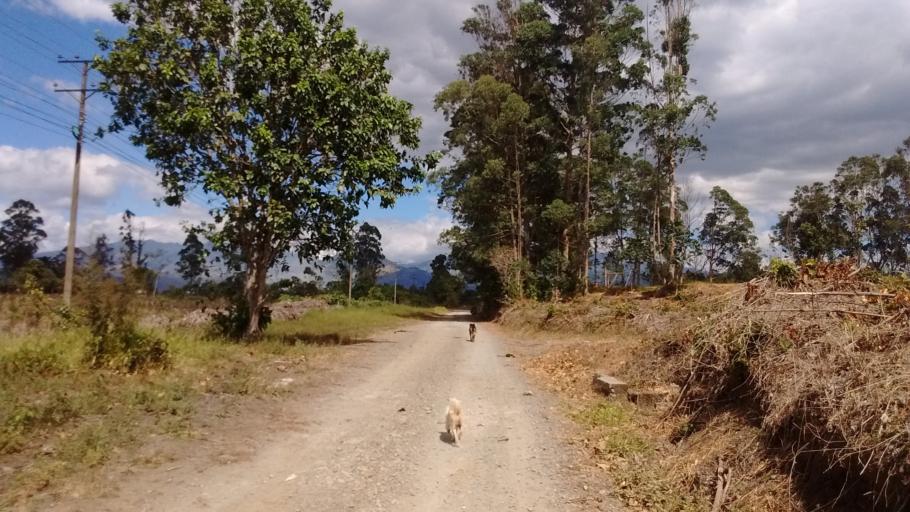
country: CO
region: Cauca
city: Popayan
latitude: 2.4967
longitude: -76.5923
